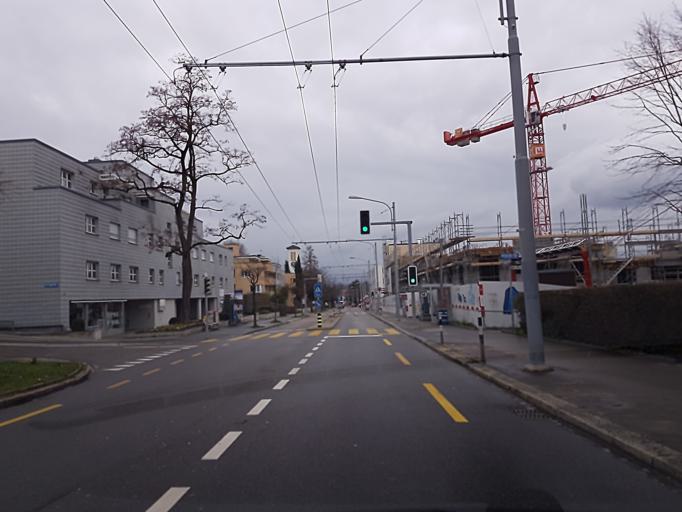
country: CH
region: Zurich
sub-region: Bezirk Zuerich
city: Zuerich (Kreis 3)
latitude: 47.3592
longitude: 8.5077
